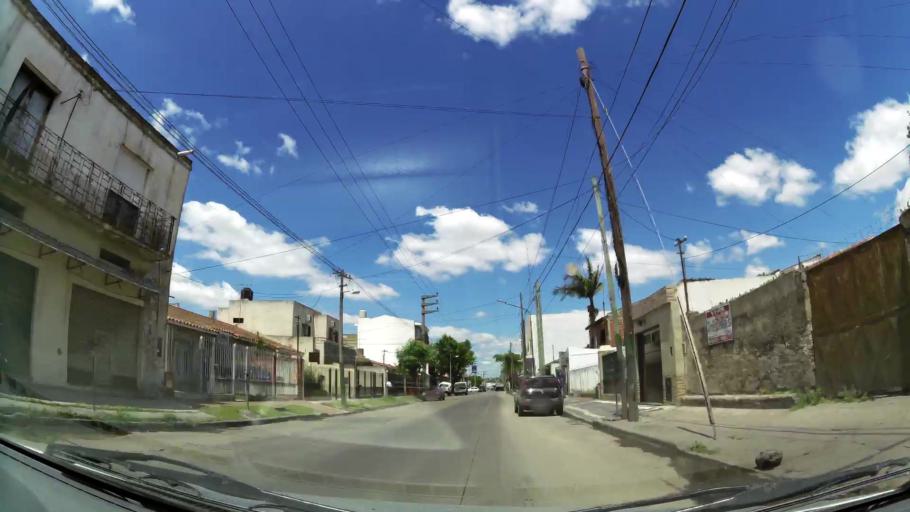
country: AR
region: Buenos Aires
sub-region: Partido de Lomas de Zamora
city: Lomas de Zamora
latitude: -34.7319
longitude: -58.4206
